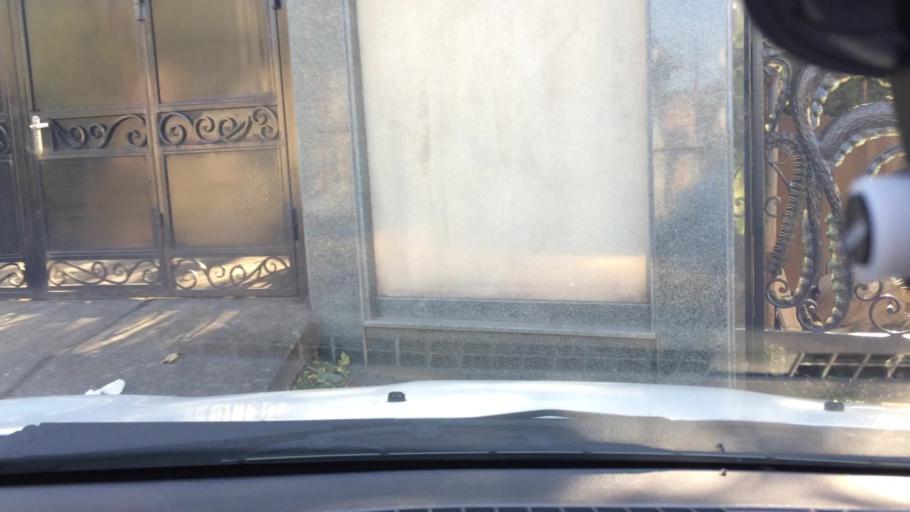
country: GE
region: Imereti
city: Kutaisi
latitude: 42.2703
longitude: 42.7101
